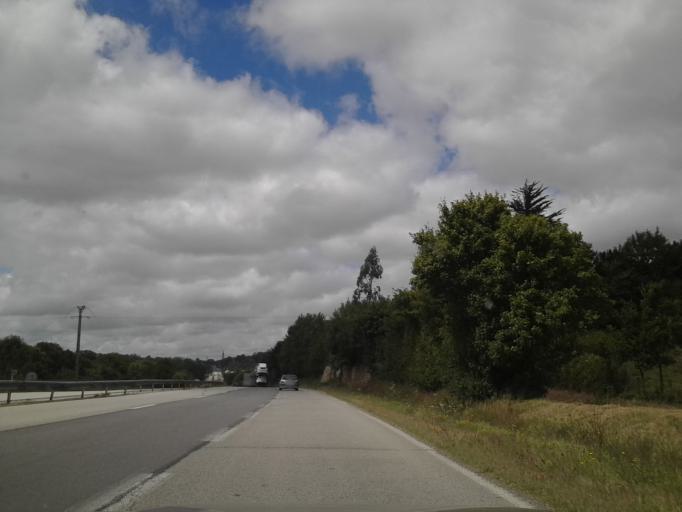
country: FR
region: Lower Normandy
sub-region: Departement de la Manche
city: Valognes
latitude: 49.5217
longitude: -1.5010
